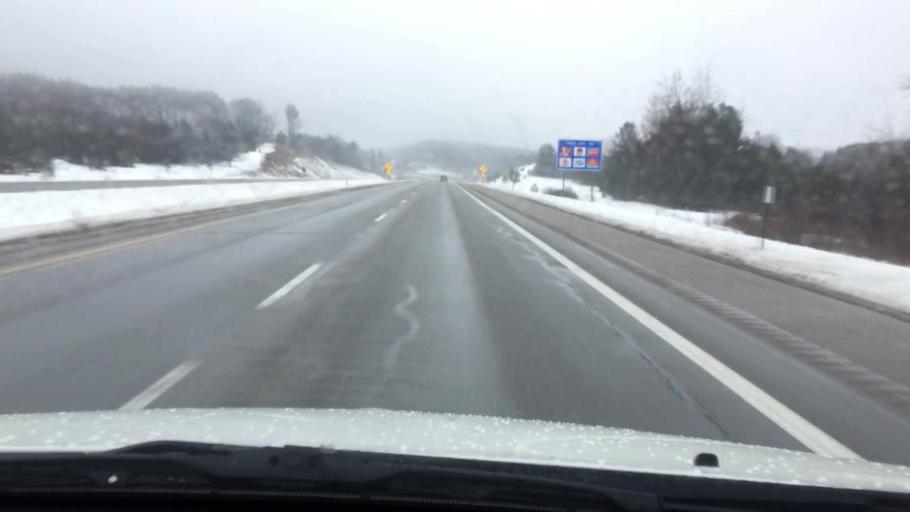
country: US
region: Michigan
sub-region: Wexford County
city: Cadillac
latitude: 44.3068
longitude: -85.3925
